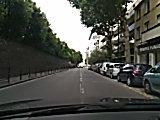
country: FR
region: Ile-de-France
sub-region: Departement des Hauts-de-Seine
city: Montrouge
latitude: 48.8100
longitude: 2.3157
